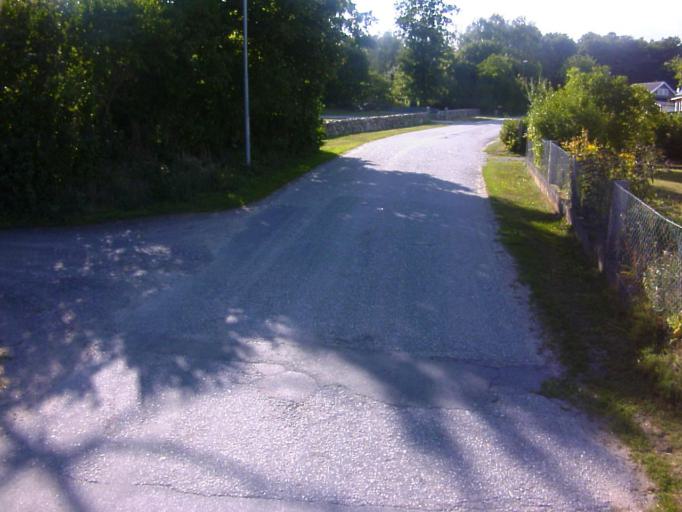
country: SE
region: Blekinge
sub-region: Solvesborgs Kommun
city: Soelvesborg
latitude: 56.0322
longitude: 14.6979
